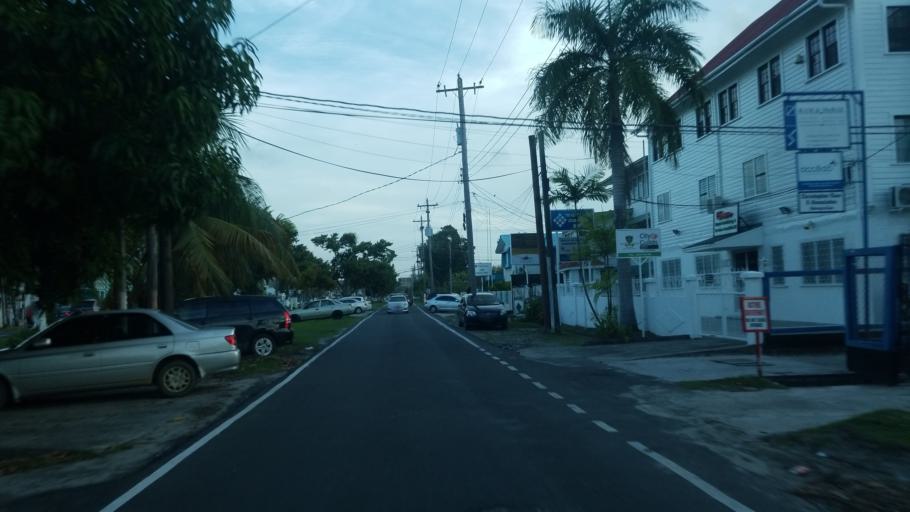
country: GY
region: Demerara-Mahaica
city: Georgetown
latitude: 6.8182
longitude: -58.1605
